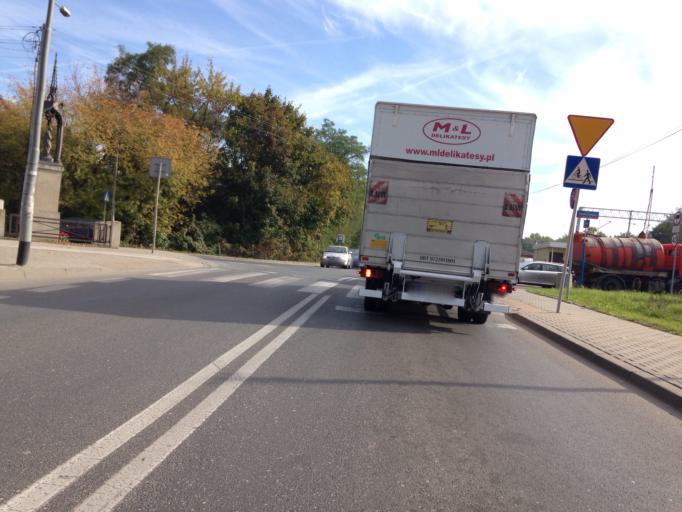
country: PL
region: Masovian Voivodeship
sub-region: Warszawa
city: Rembertow
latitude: 52.2589
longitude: 21.1263
